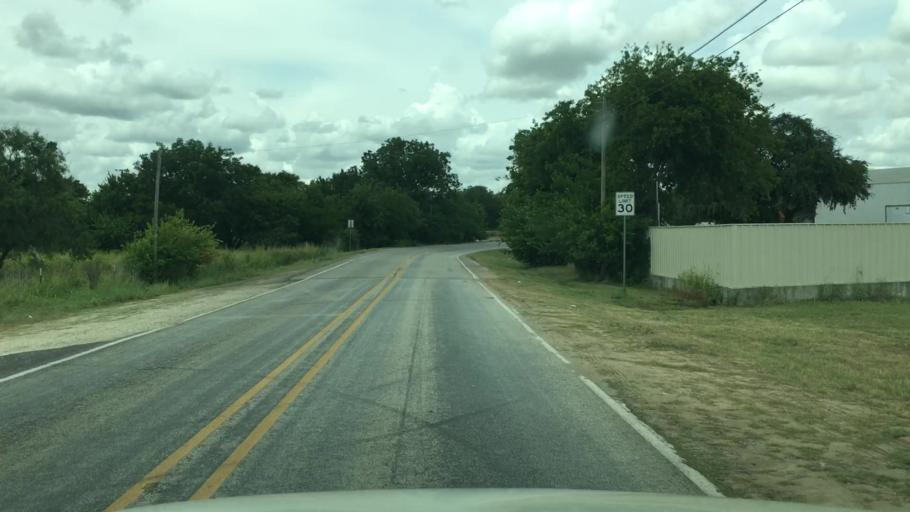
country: US
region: Texas
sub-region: McCulloch County
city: Brady
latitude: 31.1230
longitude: -99.3253
